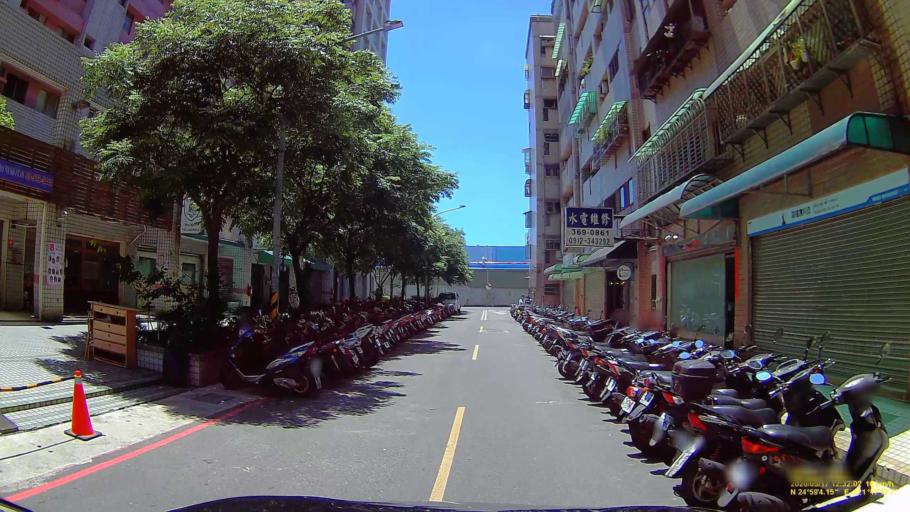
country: TW
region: Taiwan
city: Taoyuan City
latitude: 24.9845
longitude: 121.2882
